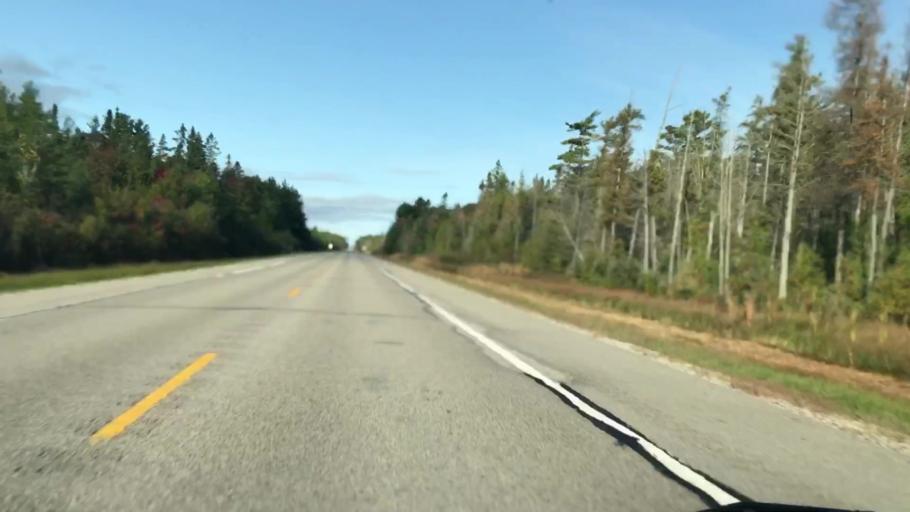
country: US
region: Michigan
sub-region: Luce County
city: Newberry
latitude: 46.3035
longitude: -85.3303
